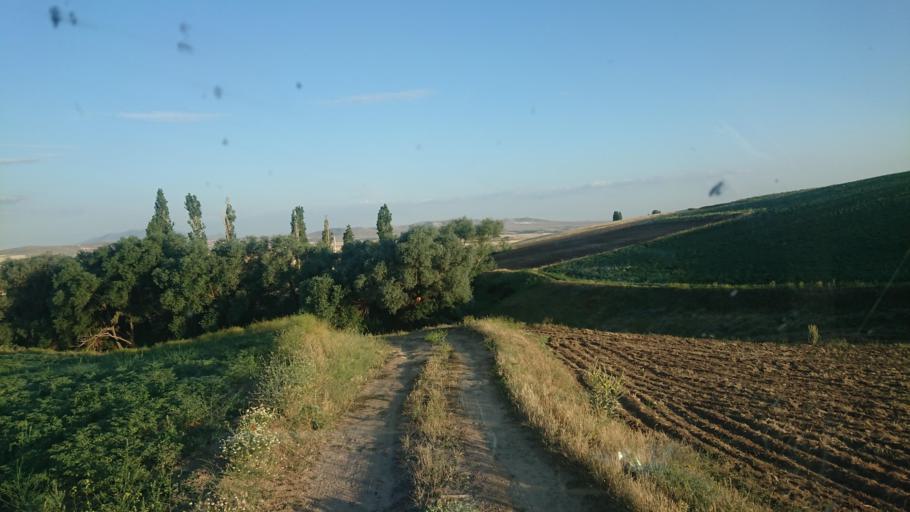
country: TR
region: Aksaray
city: Agacoren
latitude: 38.8304
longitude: 33.8867
